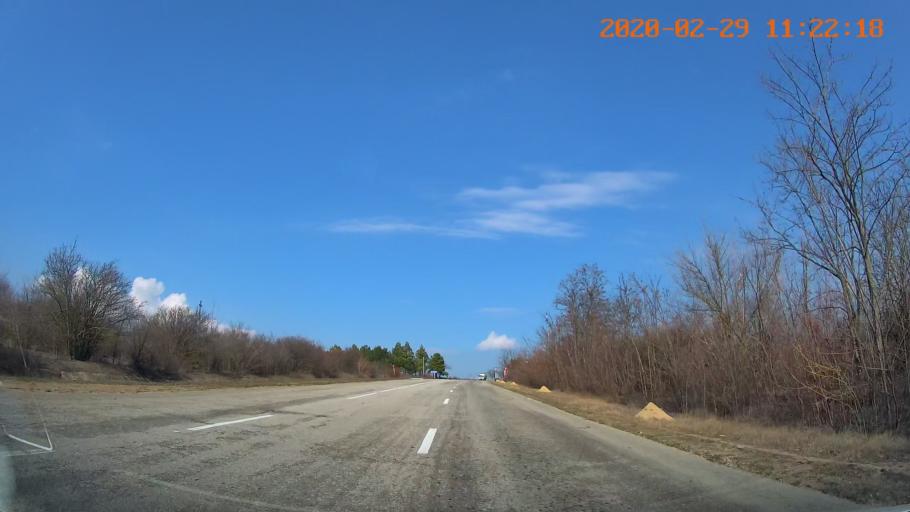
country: MD
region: Telenesti
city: Cocieri
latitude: 47.3922
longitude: 29.1627
